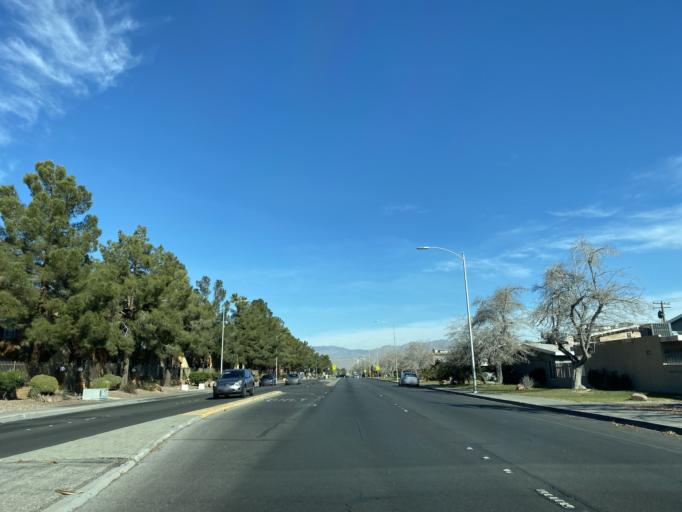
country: US
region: Nevada
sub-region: Clark County
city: Spring Valley
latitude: 36.1825
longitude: -115.2238
